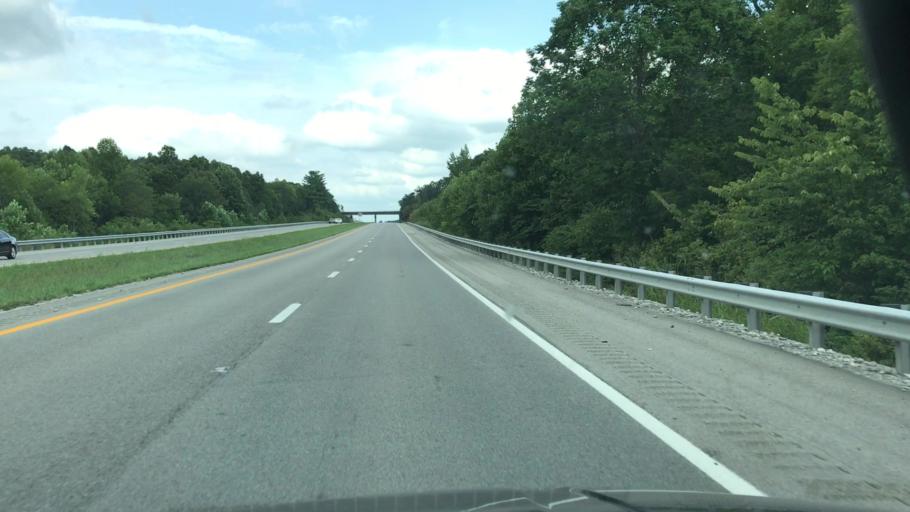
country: US
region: Kentucky
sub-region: Hopkins County
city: Dawson Springs
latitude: 37.1539
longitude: -87.7845
